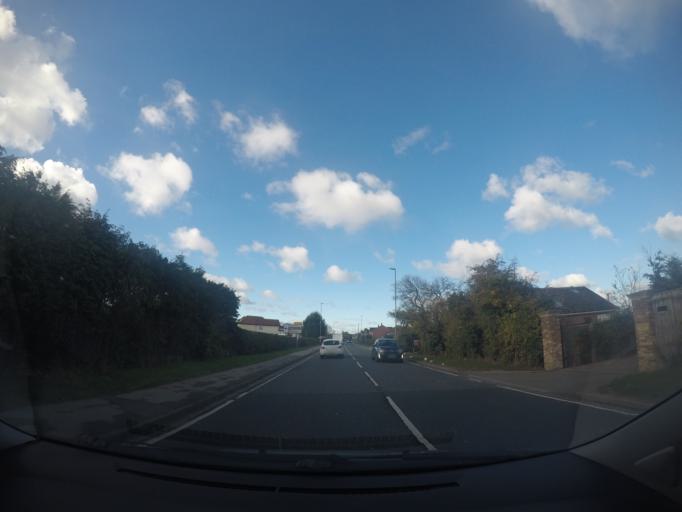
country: GB
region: England
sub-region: City and Borough of Leeds
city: Walton
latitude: 53.9991
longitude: -1.2783
